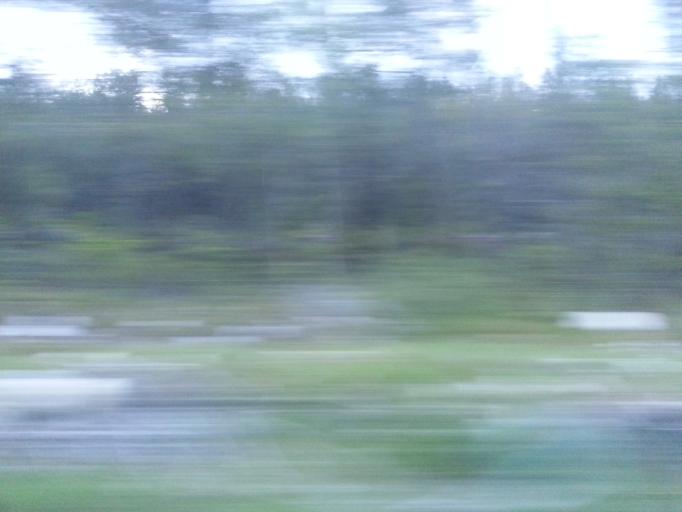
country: NO
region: Oppland
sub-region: Dovre
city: Dombas
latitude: 62.1043
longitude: 9.1184
